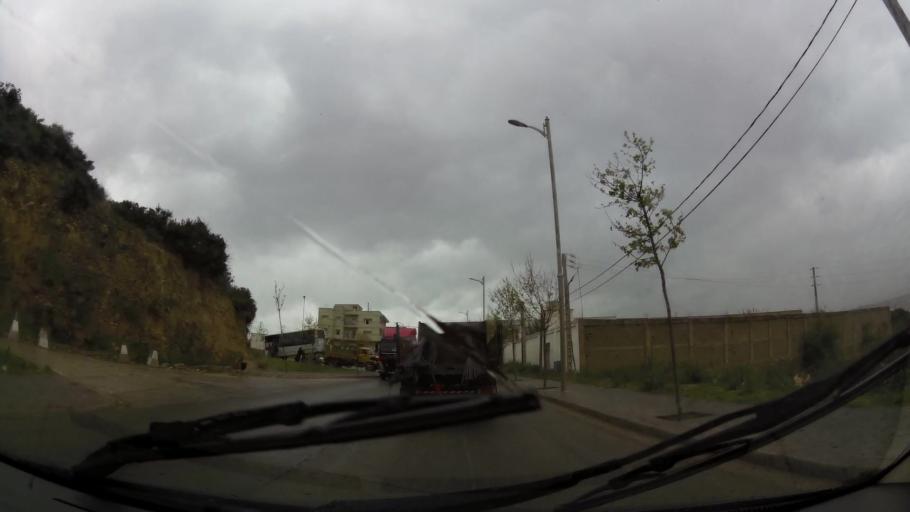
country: MA
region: Tanger-Tetouan
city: Tetouan
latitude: 35.5575
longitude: -5.4060
